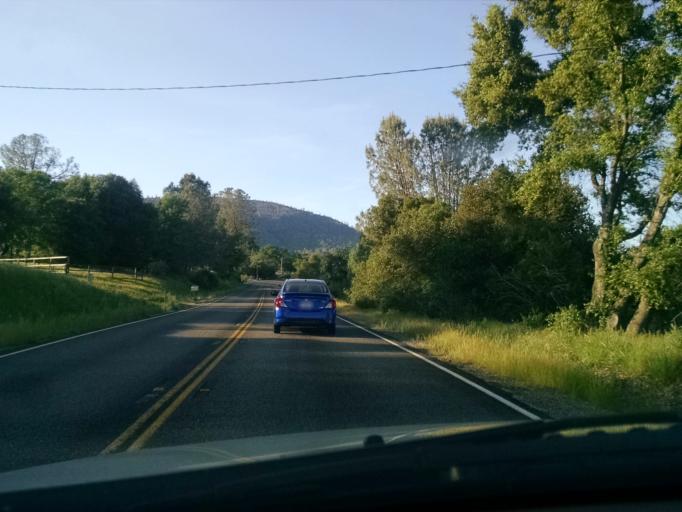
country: US
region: California
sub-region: Madera County
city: Ahwahnee
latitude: 37.3926
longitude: -119.7371
